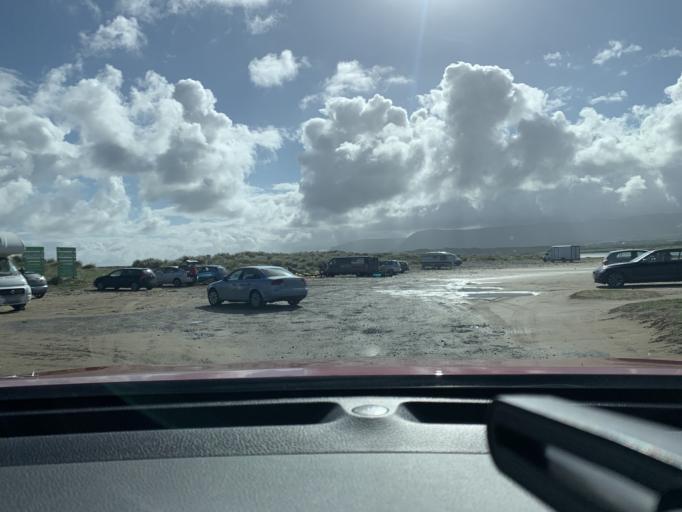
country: IE
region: Connaught
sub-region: Sligo
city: Strandhill
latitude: 54.4044
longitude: -8.5606
